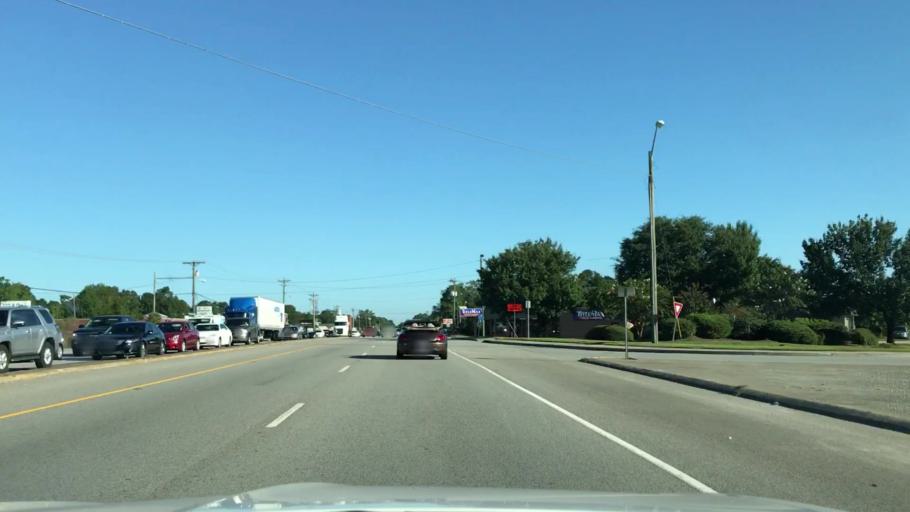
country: US
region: South Carolina
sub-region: Berkeley County
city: Goose Creek
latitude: 32.9967
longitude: -80.0390
